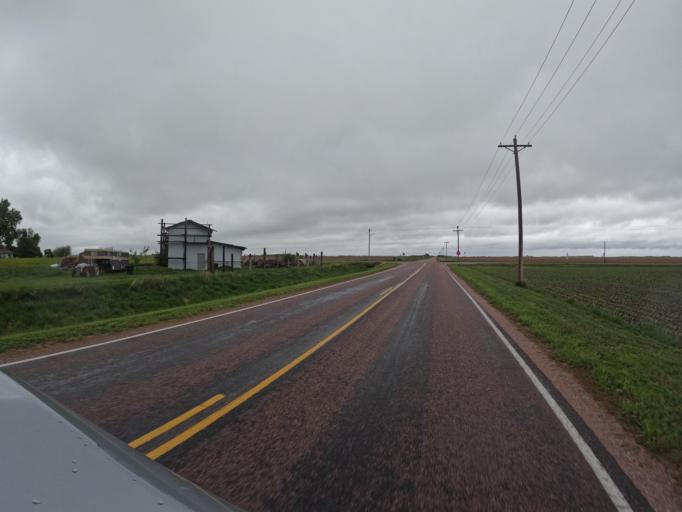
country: US
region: Nebraska
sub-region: Clay County
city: Harvard
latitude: 40.6259
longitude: -98.0906
